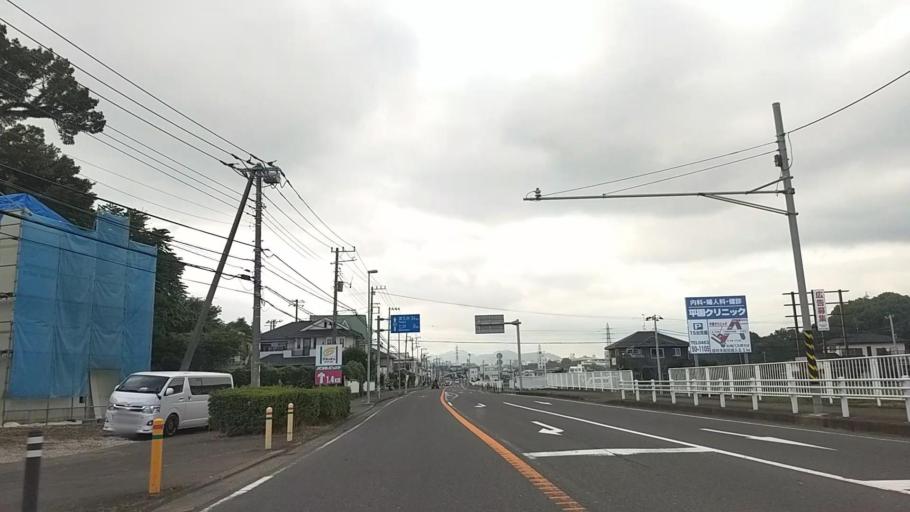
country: JP
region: Kanagawa
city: Isehara
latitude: 35.3791
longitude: 139.3179
